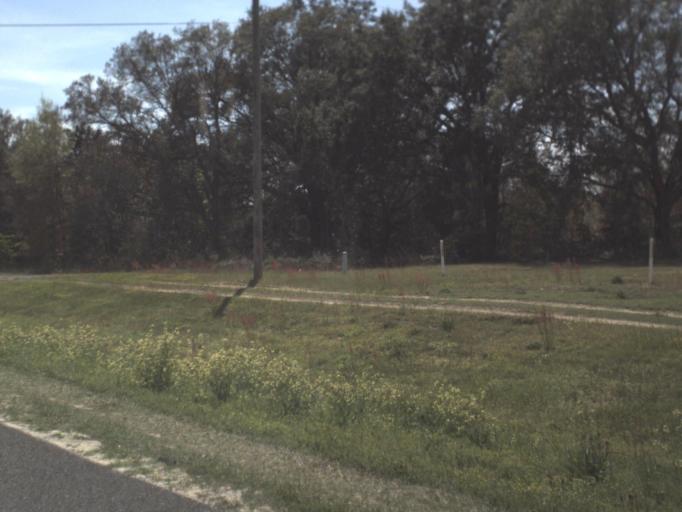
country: US
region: Florida
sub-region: Bay County
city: Lynn Haven
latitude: 30.4289
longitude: -85.6879
